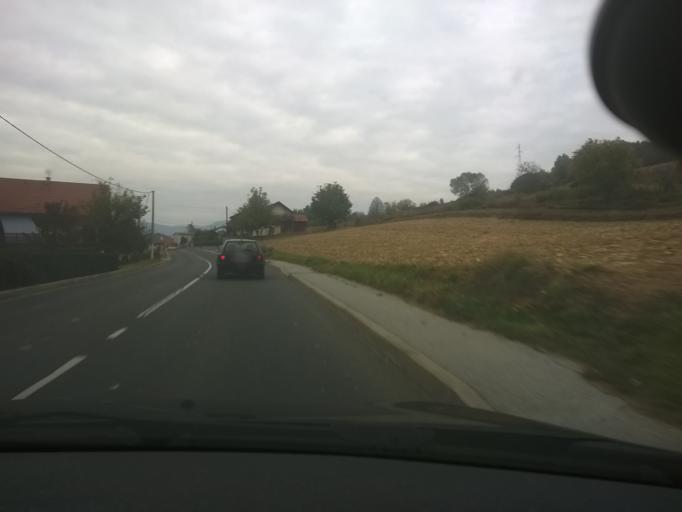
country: HR
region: Krapinsko-Zagorska
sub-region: Grad Krapina
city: Krapina
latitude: 46.1214
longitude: 15.8946
